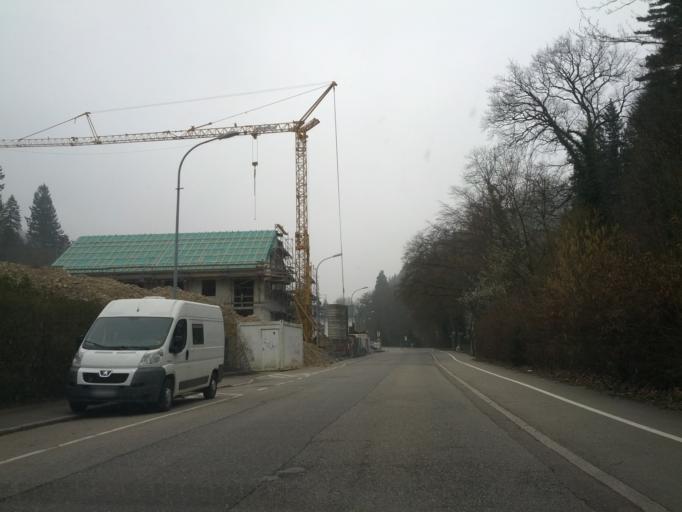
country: DE
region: Baden-Wuerttemberg
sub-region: Freiburg Region
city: Horben
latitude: 47.9589
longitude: 7.8638
